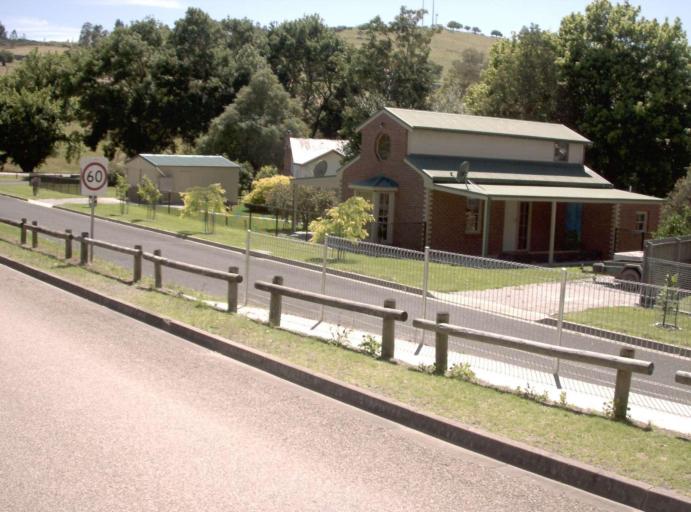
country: AU
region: Victoria
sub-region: East Gippsland
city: Lakes Entrance
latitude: -37.4959
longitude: 148.1736
